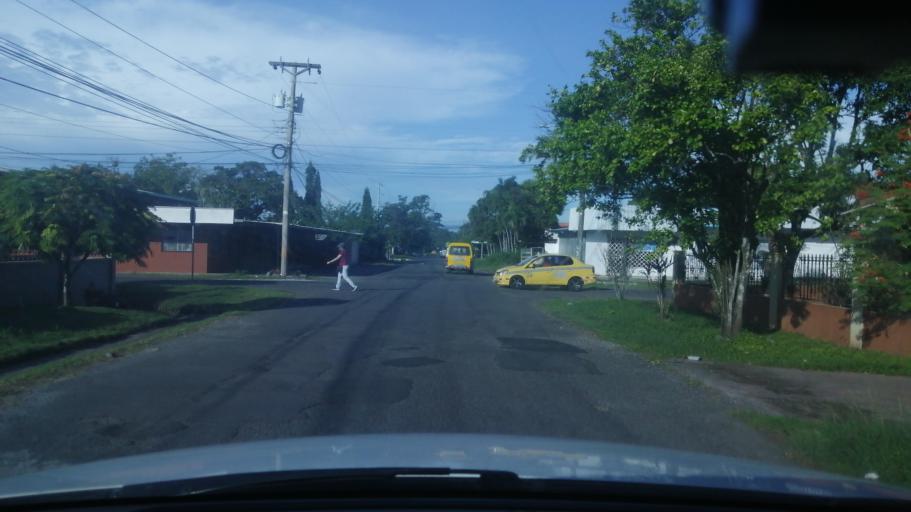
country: PA
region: Chiriqui
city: David
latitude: 8.4349
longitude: -82.4344
